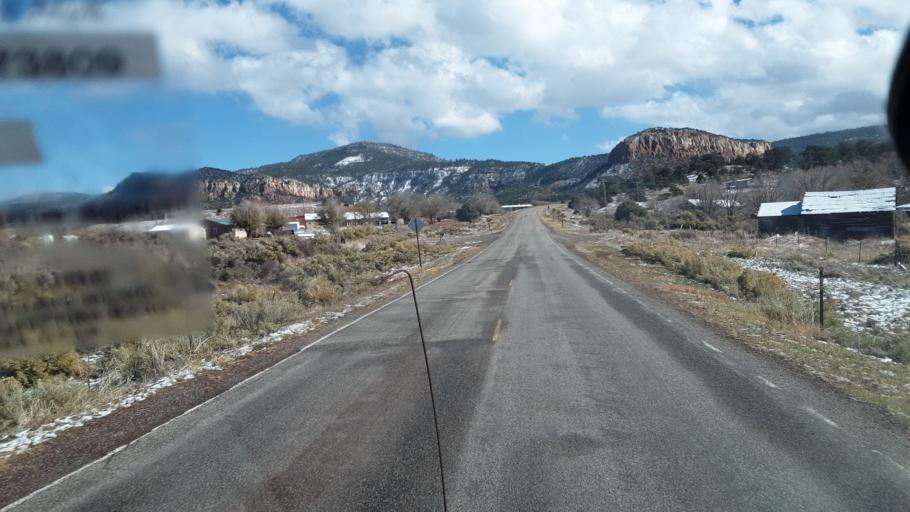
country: US
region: New Mexico
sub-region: Rio Arriba County
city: Santa Teresa
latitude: 36.2301
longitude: -106.8107
